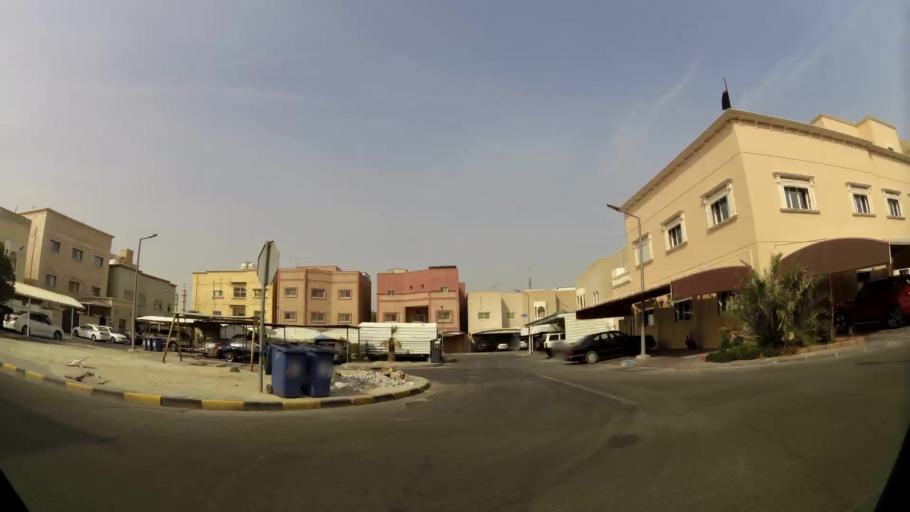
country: KW
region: Al Asimah
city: Ar Rabiyah
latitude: 29.2857
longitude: 47.9451
